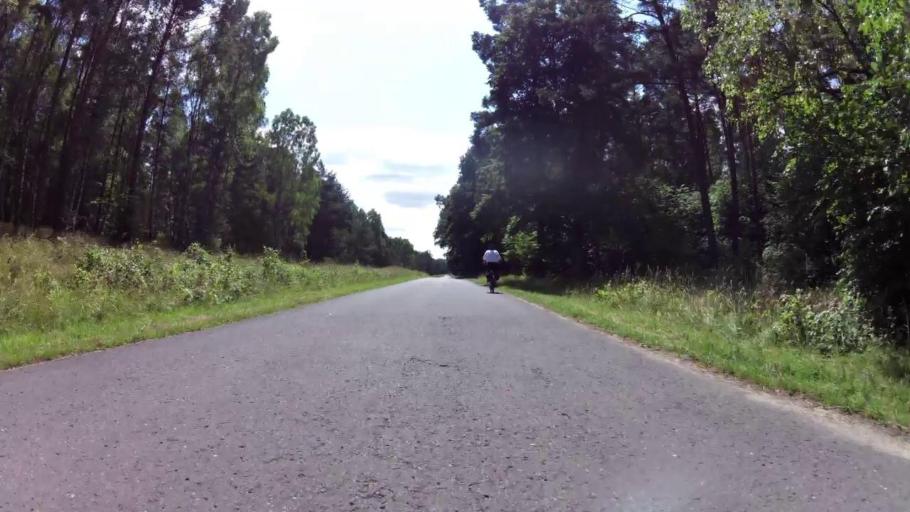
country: PL
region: West Pomeranian Voivodeship
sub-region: Powiat drawski
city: Drawsko Pomorskie
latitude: 53.3844
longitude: 15.7289
